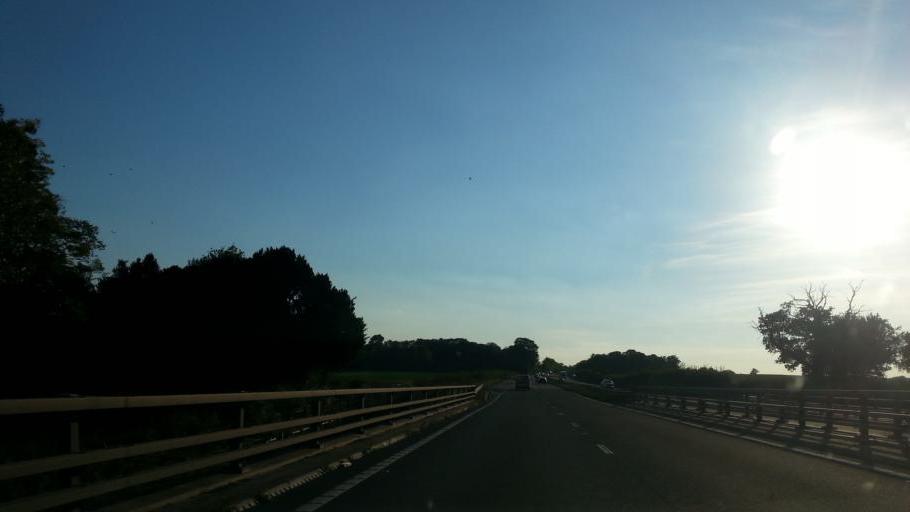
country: GB
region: England
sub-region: Worcestershire
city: Upton upon Severn
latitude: 52.0246
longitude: -2.2081
